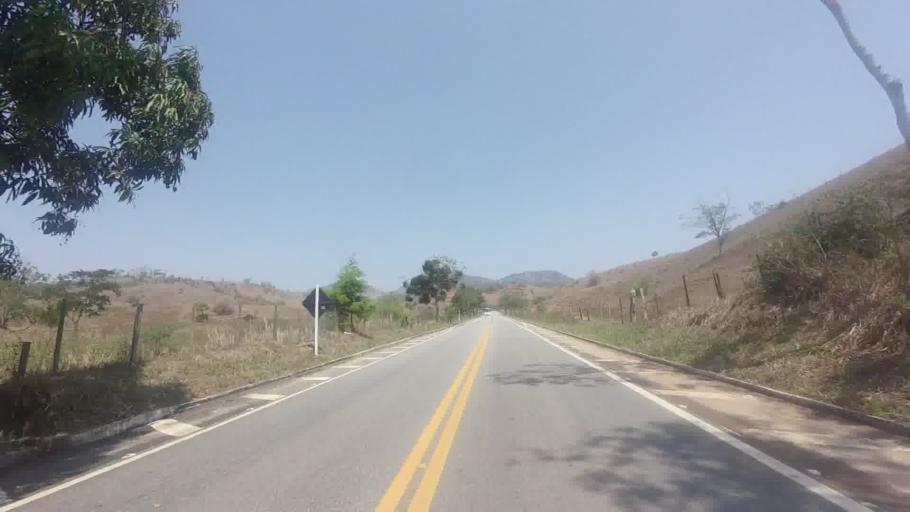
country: BR
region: Espirito Santo
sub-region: Jeronimo Monteiro
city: Jeronimo Monteiro
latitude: -20.8790
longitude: -41.2685
